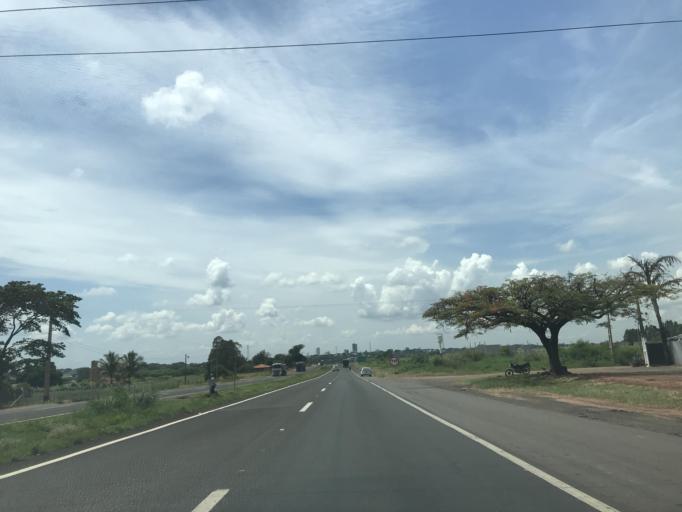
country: BR
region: Parana
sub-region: Alto Parana
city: Alto Parana
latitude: -23.1769
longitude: -52.2293
